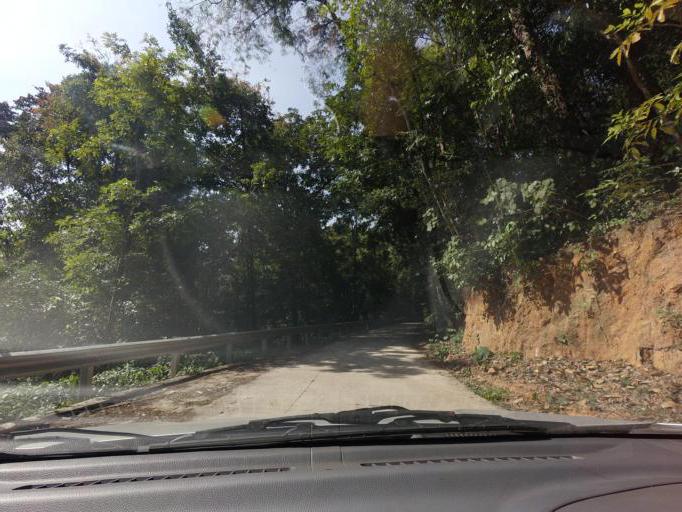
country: IN
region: Karnataka
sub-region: Kodagu
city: Somvarpet
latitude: 12.6982
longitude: 75.6314
